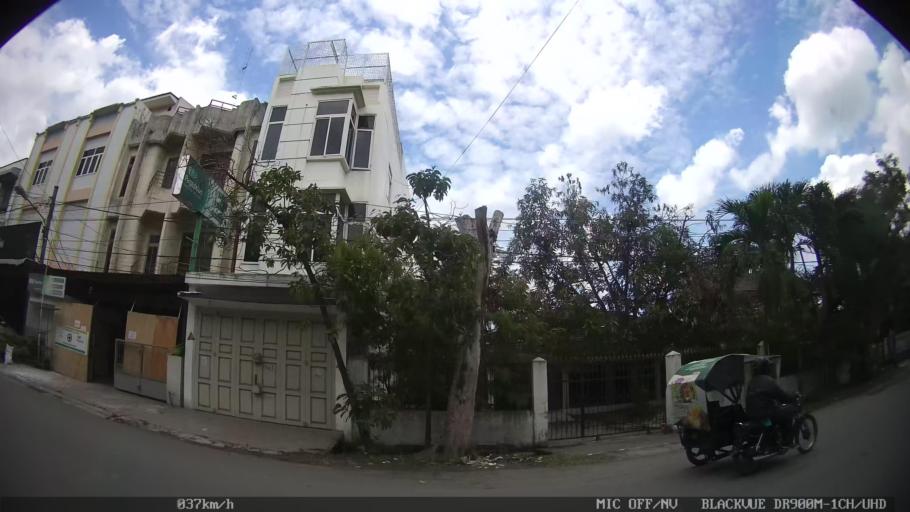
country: ID
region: North Sumatra
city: Medan
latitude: 3.5949
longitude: 98.7072
